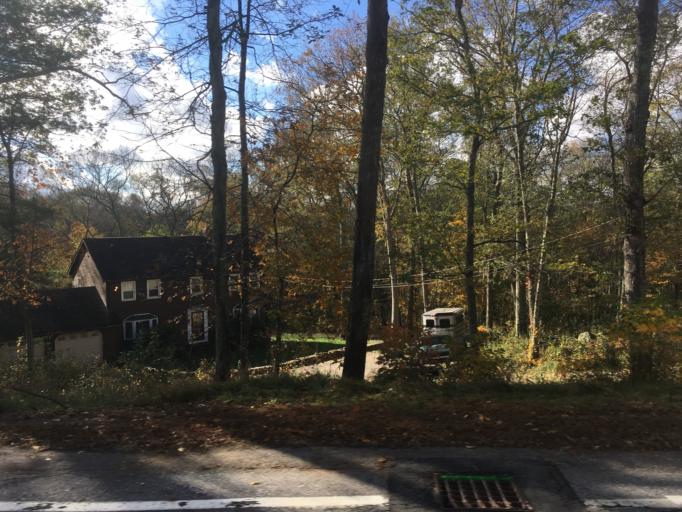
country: US
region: Rhode Island
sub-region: Providence County
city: North Scituate
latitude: 41.7921
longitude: -71.6142
